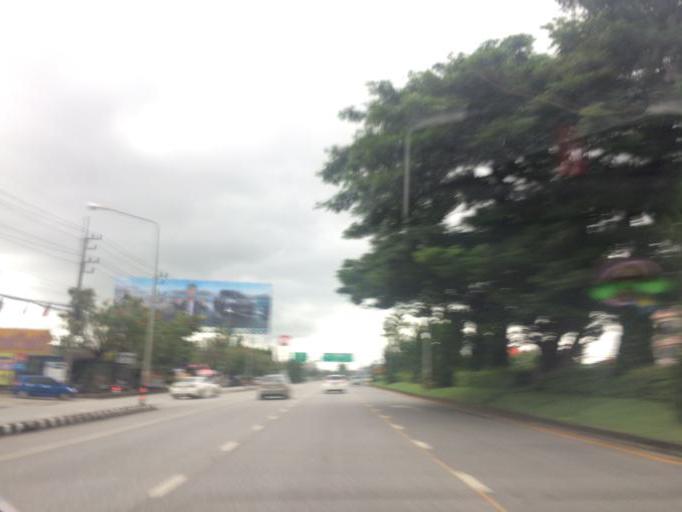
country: TH
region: Chiang Rai
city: Chiang Rai
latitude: 19.8949
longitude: 99.8380
